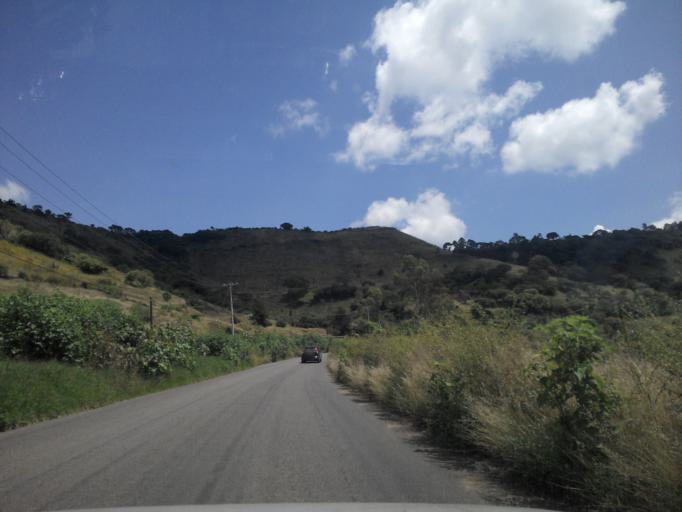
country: MX
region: Jalisco
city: Atotonilco el Alto
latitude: 20.5704
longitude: -102.5125
